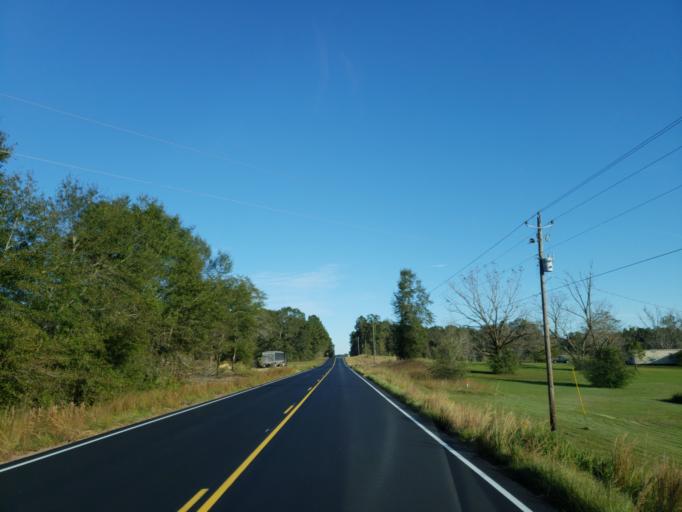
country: US
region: Mississippi
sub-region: Perry County
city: Richton
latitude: 31.3712
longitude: -88.8234
